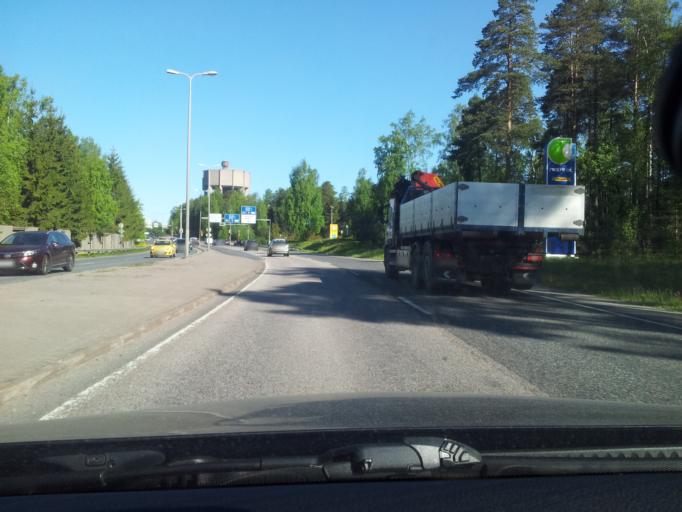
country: FI
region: Uusimaa
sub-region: Helsinki
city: Otaniemi
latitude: 60.1781
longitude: 24.8262
